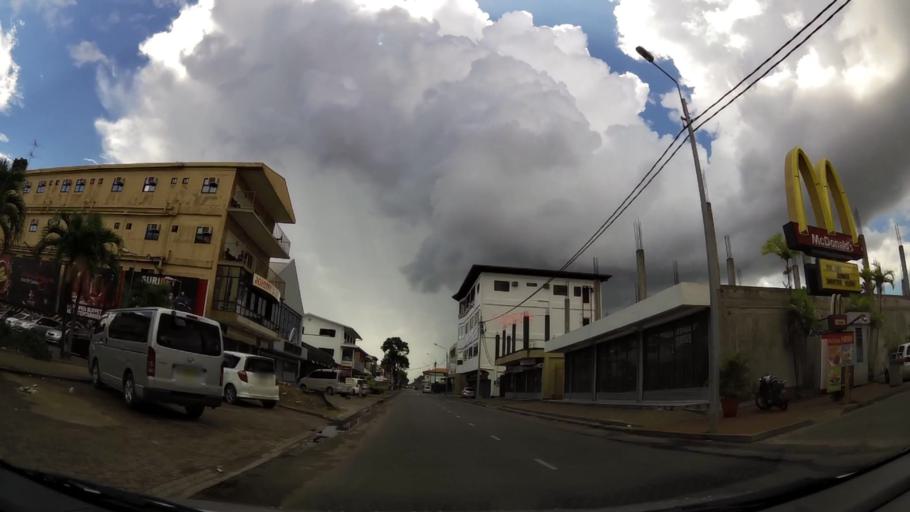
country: SR
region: Paramaribo
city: Paramaribo
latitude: 5.8274
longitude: -55.1581
